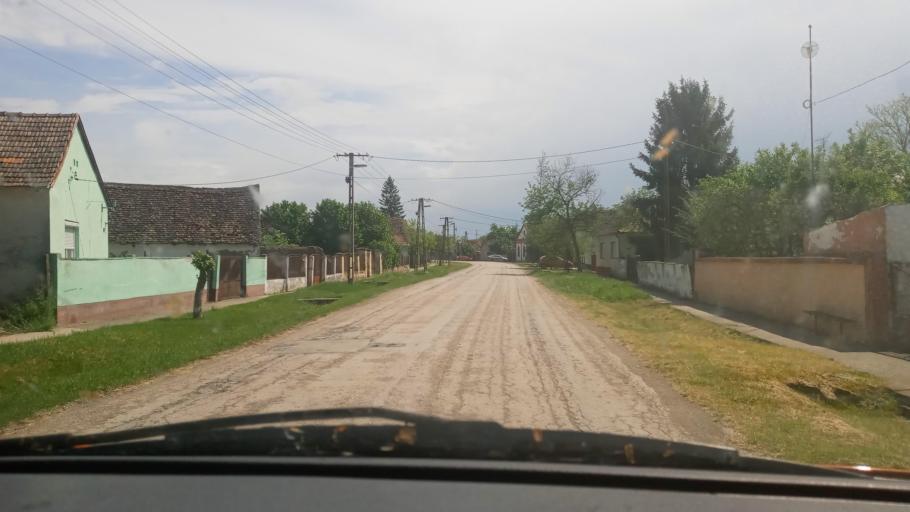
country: HU
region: Baranya
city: Beremend
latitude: 45.7922
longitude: 18.3505
